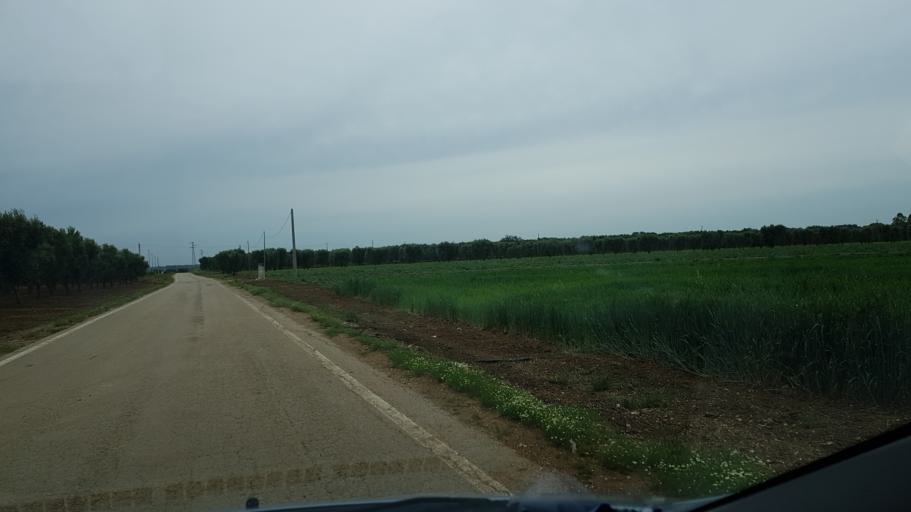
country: IT
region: Apulia
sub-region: Provincia di Brindisi
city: San Vito dei Normanni
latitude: 40.6659
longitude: 17.8094
